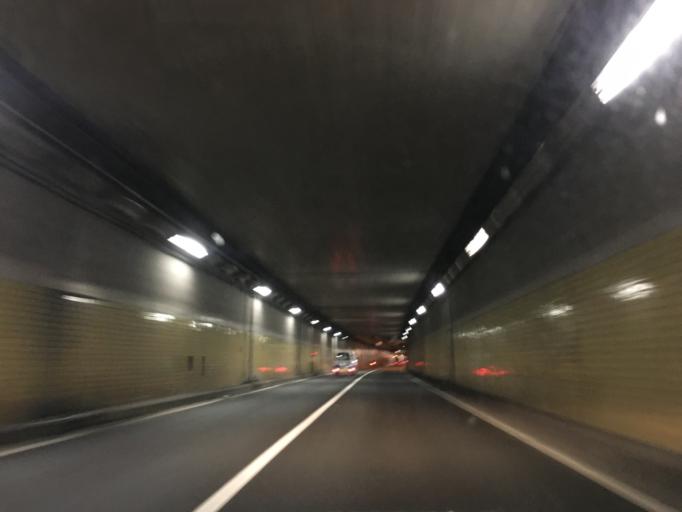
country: JP
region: Tokyo
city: Tokyo
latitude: 35.6799
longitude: 139.7196
